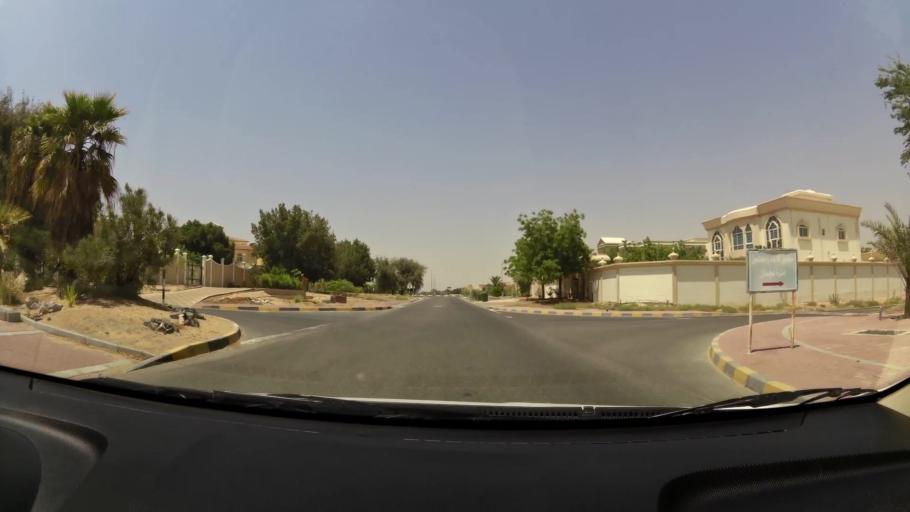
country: AE
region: Ajman
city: Ajman
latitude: 25.4207
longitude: 55.5069
